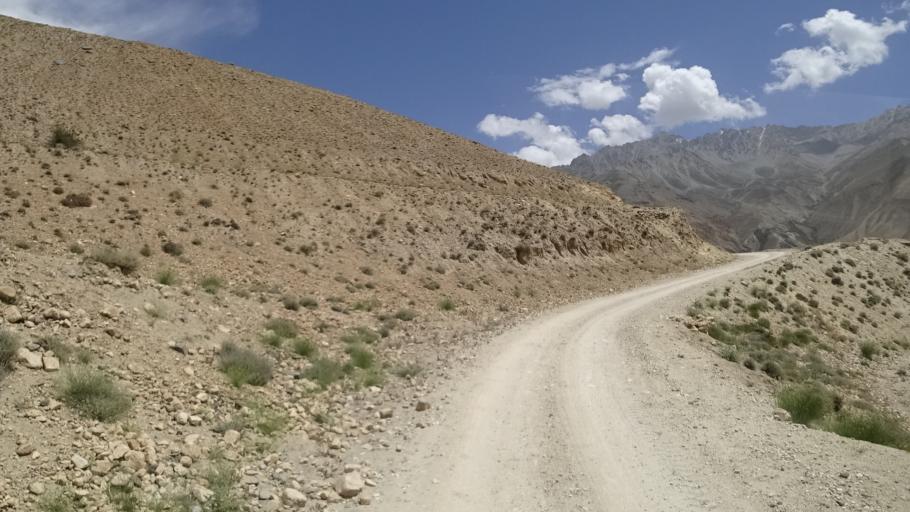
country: AF
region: Badakhshan
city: Khandud
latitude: 37.0832
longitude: 72.6973
